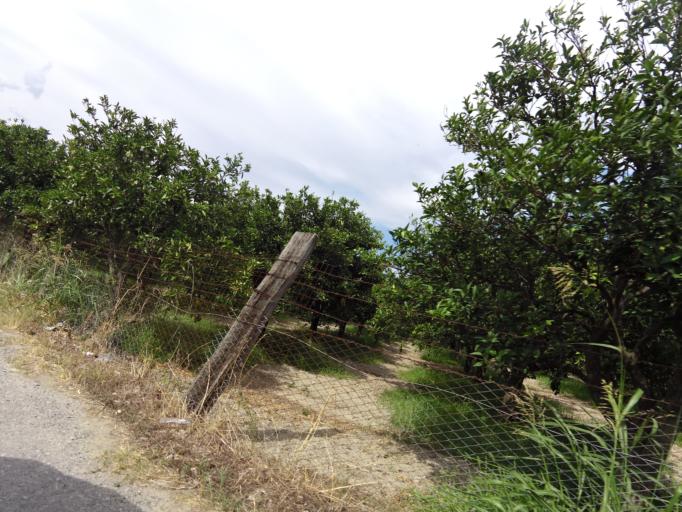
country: IT
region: Calabria
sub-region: Provincia di Reggio Calabria
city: Monasterace
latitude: 38.4554
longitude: 16.5159
